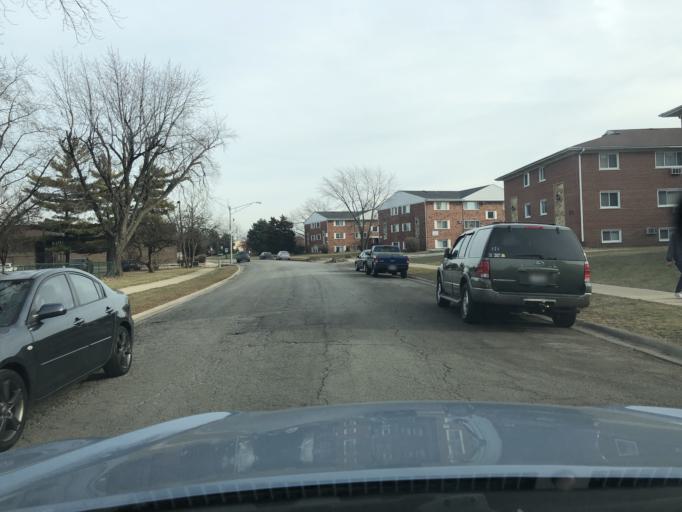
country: US
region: Illinois
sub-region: DuPage County
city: Addison
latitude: 41.9247
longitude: -87.9930
